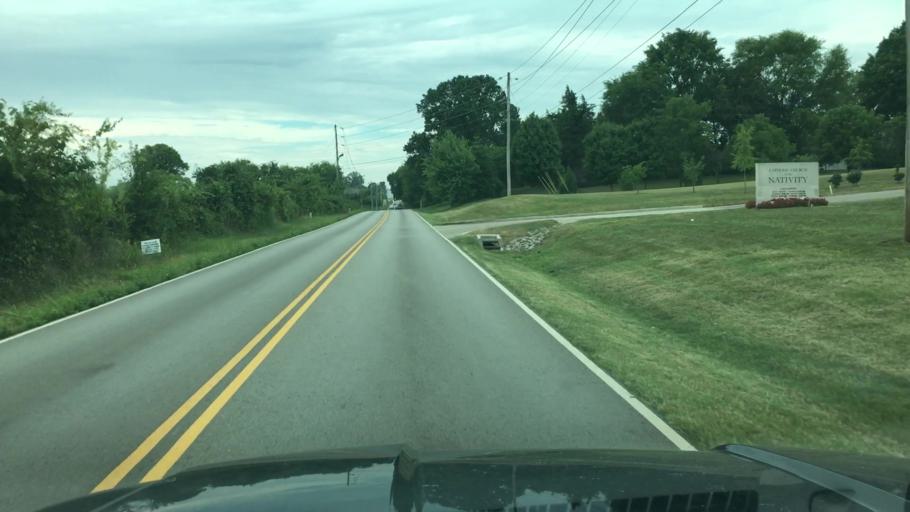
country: US
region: Tennessee
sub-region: Williamson County
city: Thompson's Station
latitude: 35.7660
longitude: -86.8816
